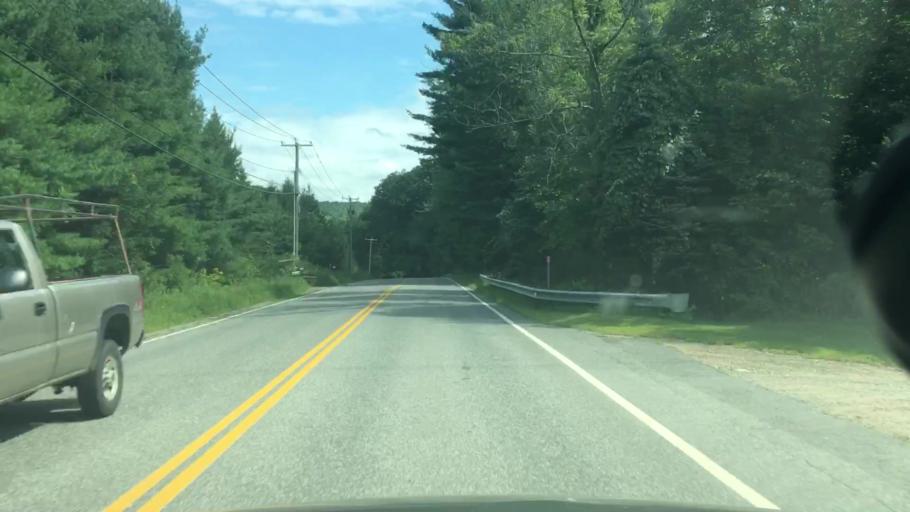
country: US
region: Massachusetts
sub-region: Franklin County
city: Shelburne
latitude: 42.6312
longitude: -72.6683
